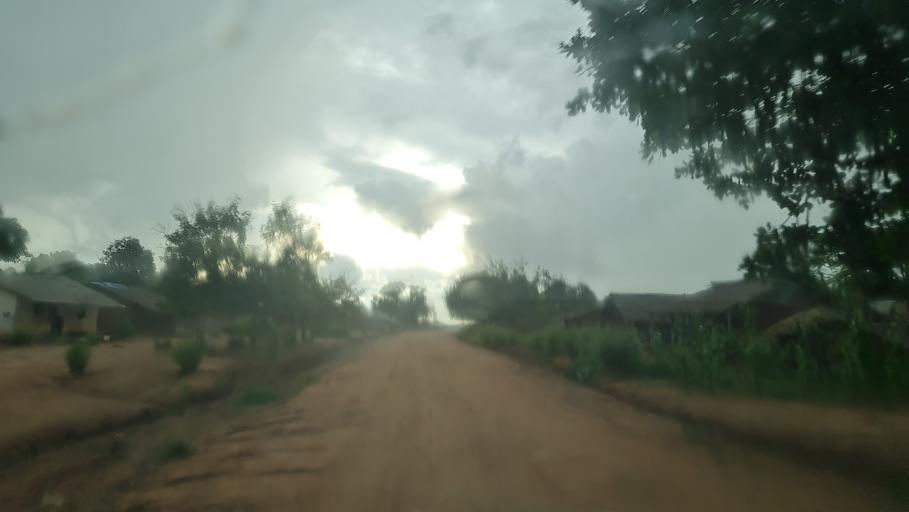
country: MZ
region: Nampula
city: Nacala
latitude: -14.0041
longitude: 40.3517
